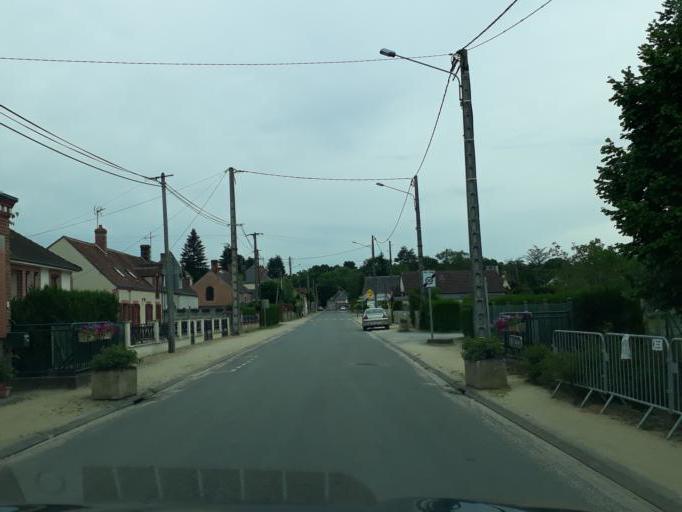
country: FR
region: Centre
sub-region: Departement du Loiret
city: Saint-Pere-sur-Loire
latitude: 47.7277
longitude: 2.3017
